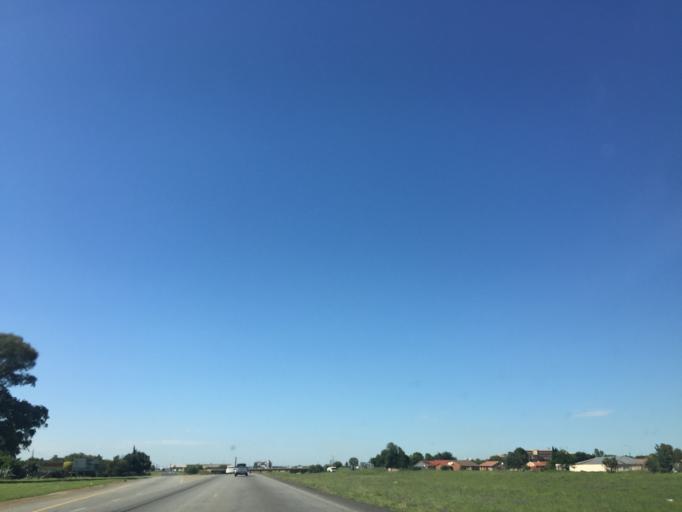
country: ZA
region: Gauteng
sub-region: Sedibeng District Municipality
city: Meyerton
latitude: -26.5559
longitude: 28.0019
